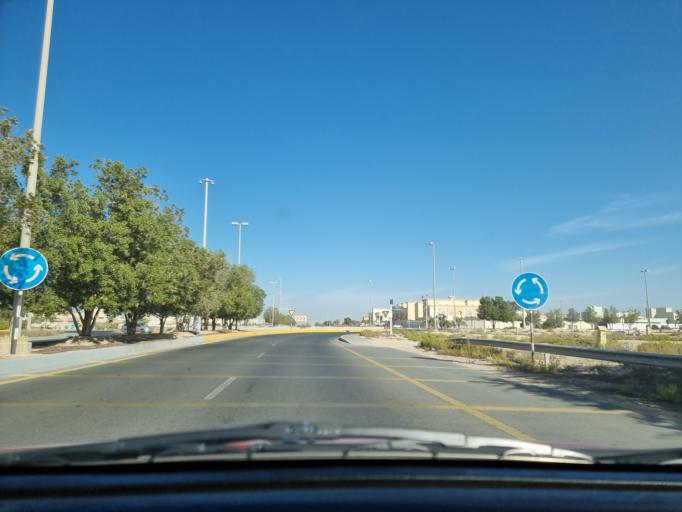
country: AE
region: Abu Dhabi
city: Abu Dhabi
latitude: 24.3844
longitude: 54.6957
